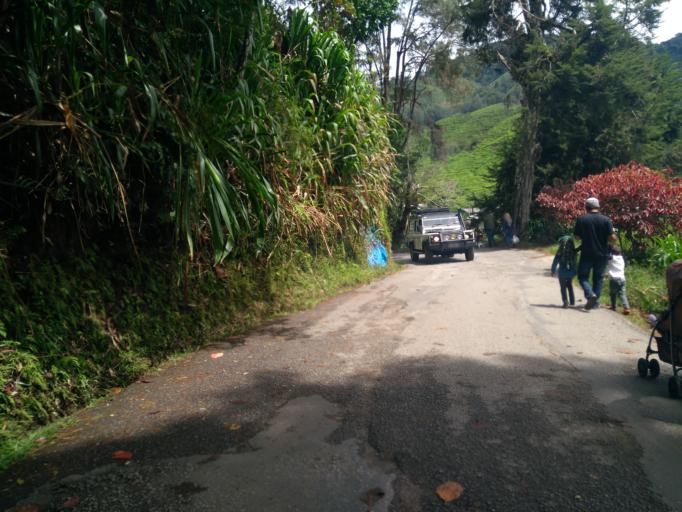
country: MY
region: Pahang
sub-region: Cameron Highlands
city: Tanah Rata
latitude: 4.5157
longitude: 101.4143
